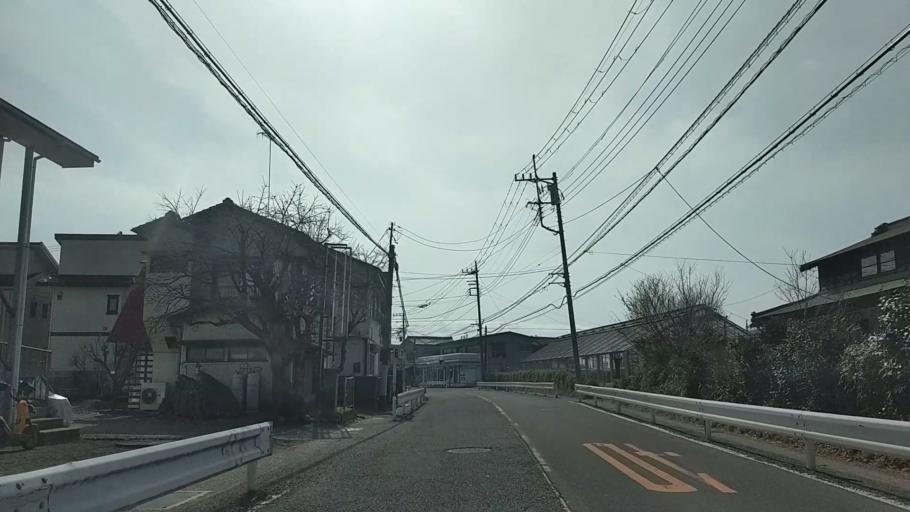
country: JP
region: Kanagawa
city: Atsugi
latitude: 35.3834
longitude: 139.3806
